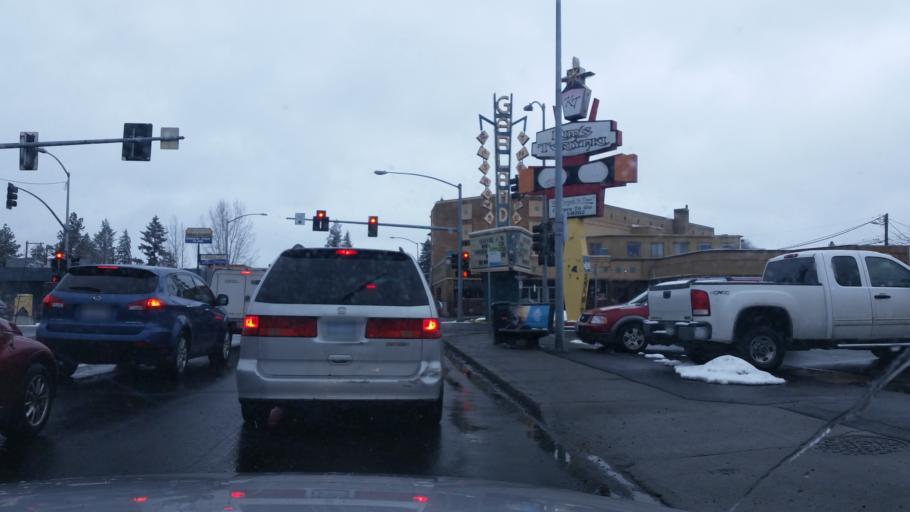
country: US
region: Washington
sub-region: Spokane County
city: Spokane
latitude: 47.6931
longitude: -117.4258
